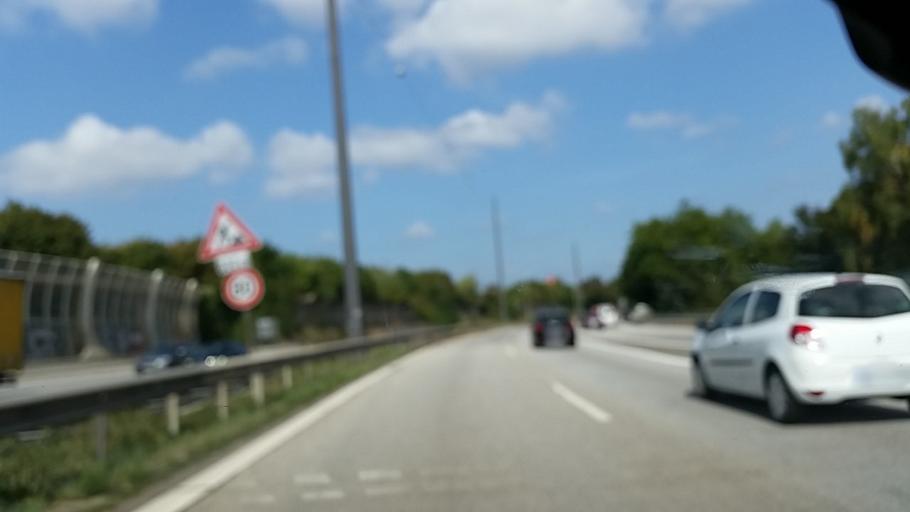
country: DE
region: Hamburg
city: Rothenburgsort
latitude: 53.5248
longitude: 10.0226
